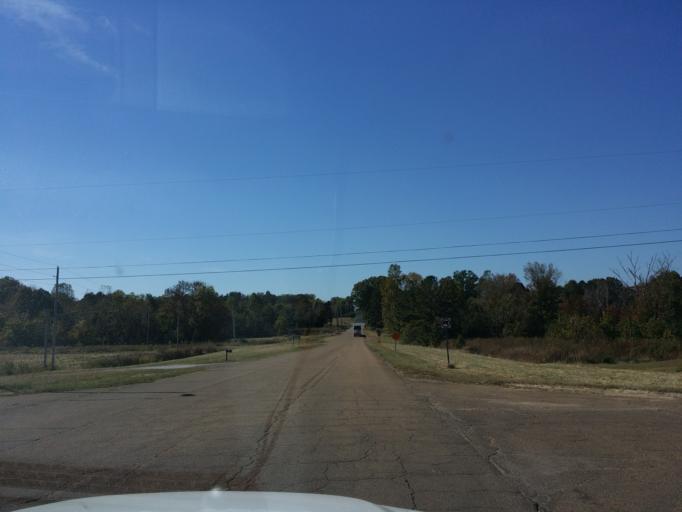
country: US
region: Mississippi
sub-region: Alcorn County
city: Corinth
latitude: 34.9819
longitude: -88.5242
